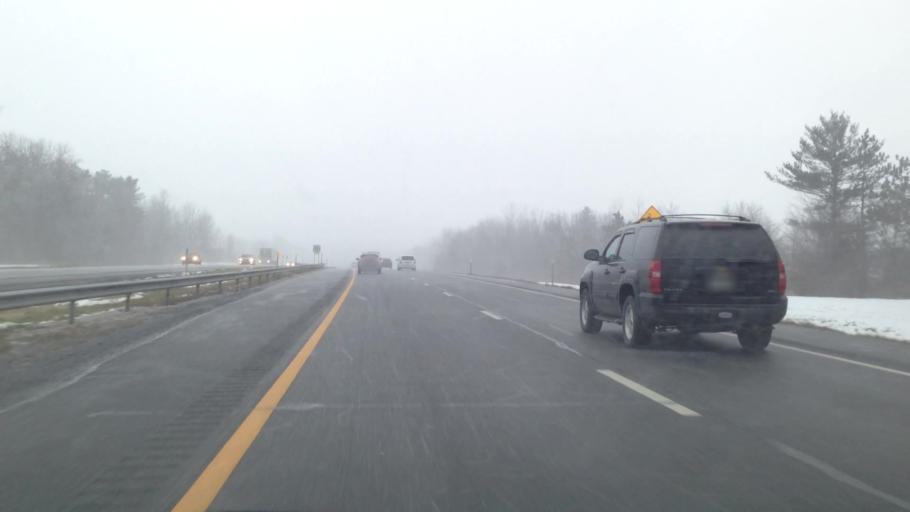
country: US
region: New York
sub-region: Montgomery County
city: Hagaman
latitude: 42.8995
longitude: -74.1079
